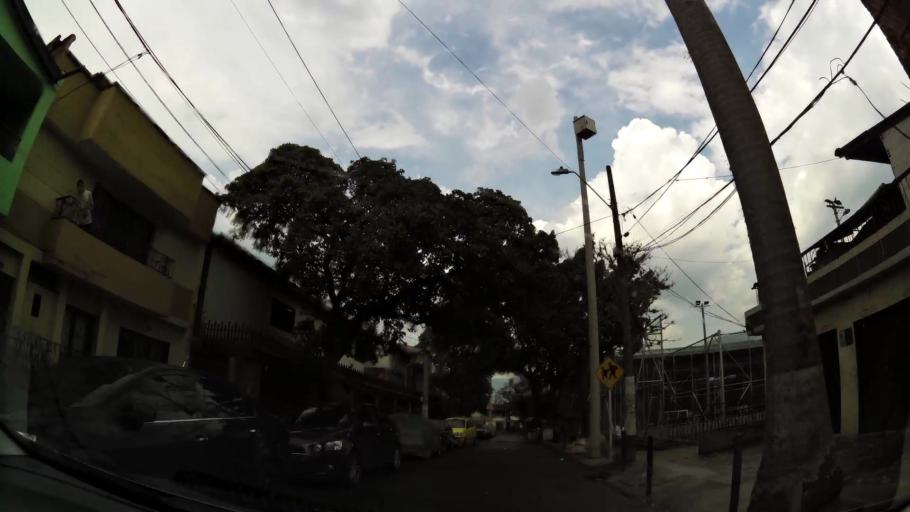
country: CO
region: Antioquia
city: Itagui
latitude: 6.1844
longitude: -75.5987
